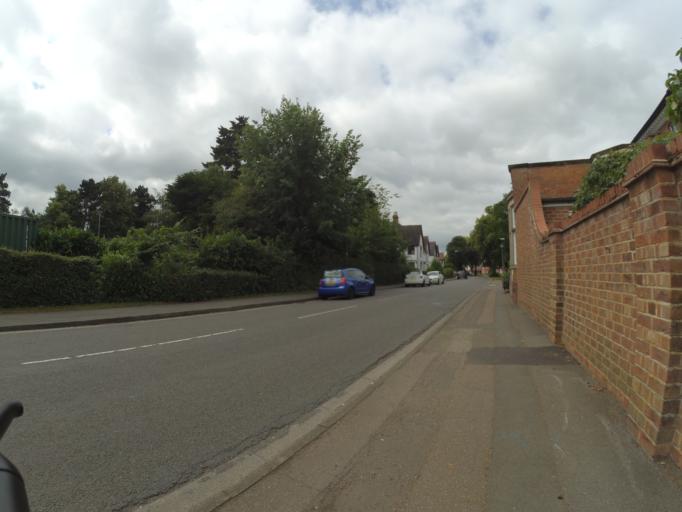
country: GB
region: England
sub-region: Warwickshire
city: Dunchurch
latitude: 52.3588
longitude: -1.2881
